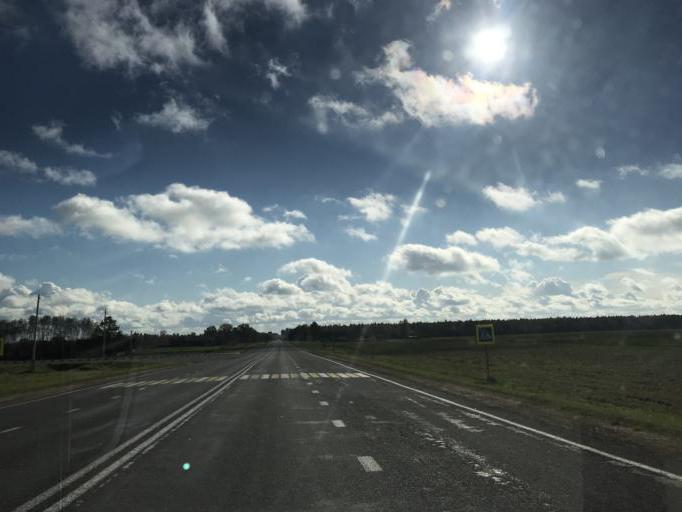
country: BY
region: Gomel
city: Dowsk
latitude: 53.1324
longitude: 30.4796
